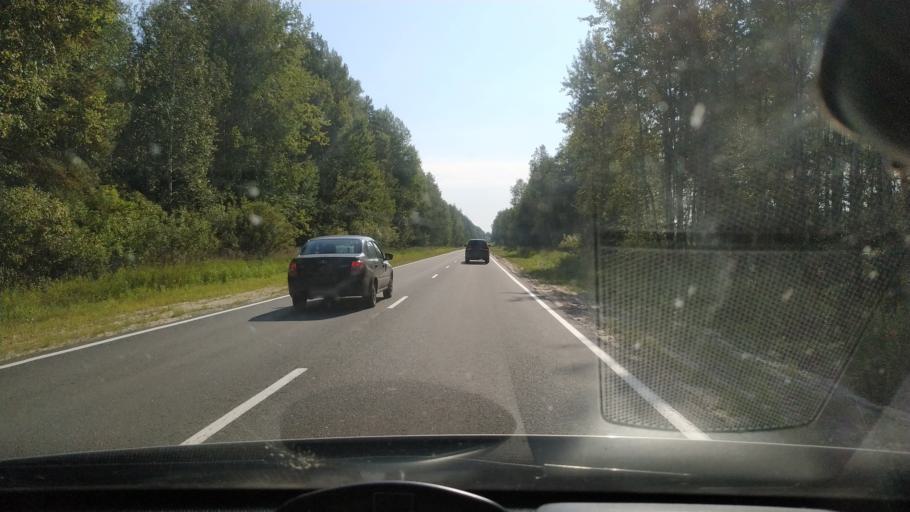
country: RU
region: Rjazan
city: Spas-Klepiki
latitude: 55.2227
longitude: 40.0772
